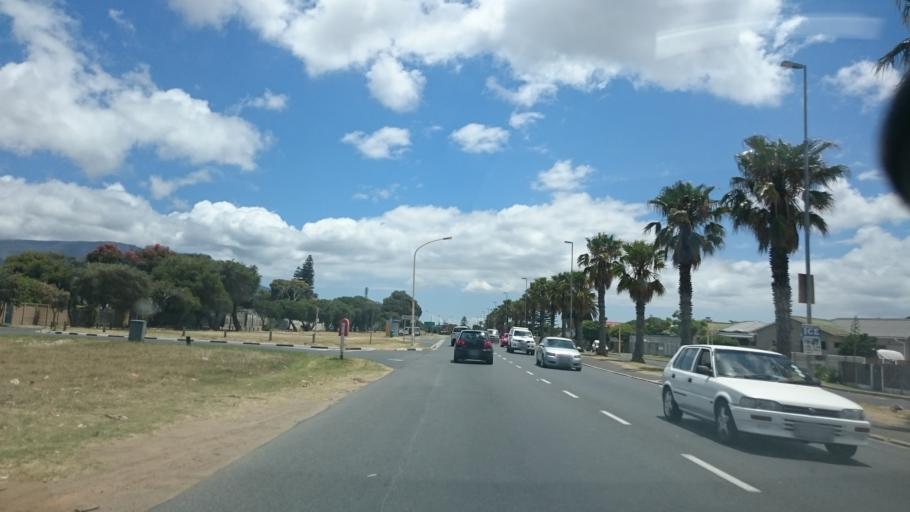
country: ZA
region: Western Cape
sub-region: City of Cape Town
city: Bergvliet
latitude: -34.0562
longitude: 18.4608
